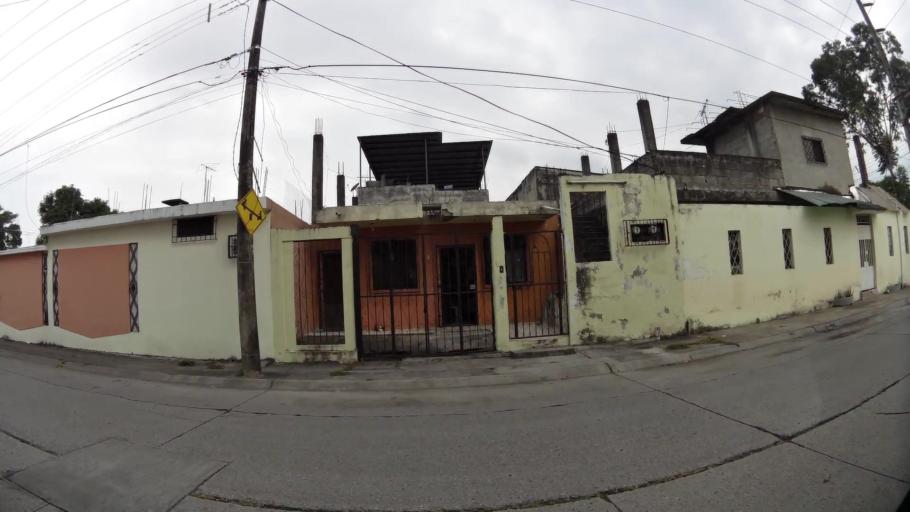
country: EC
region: Guayas
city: Eloy Alfaro
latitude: -2.1196
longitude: -79.8931
